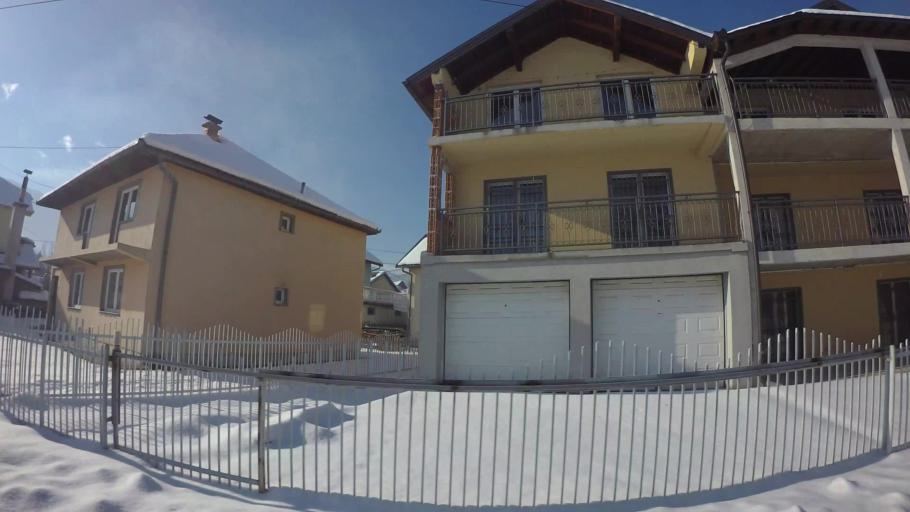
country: BA
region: Federation of Bosnia and Herzegovina
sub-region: Kanton Sarajevo
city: Sarajevo
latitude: 43.8080
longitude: 18.3176
